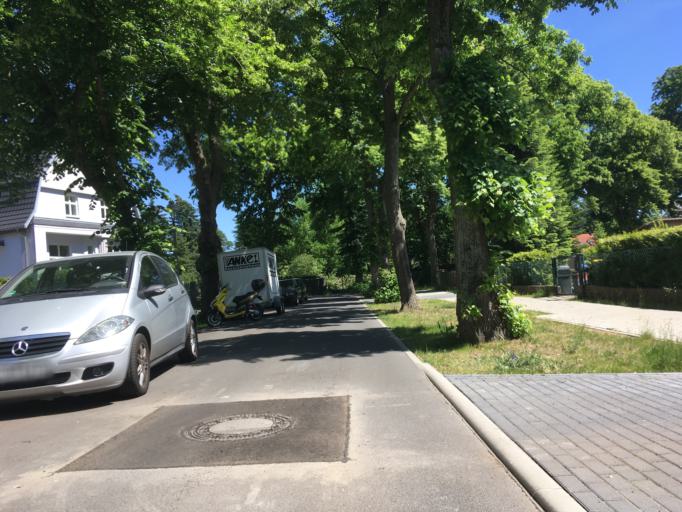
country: DE
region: Berlin
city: Schmockwitz
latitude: 52.3955
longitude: 13.6340
